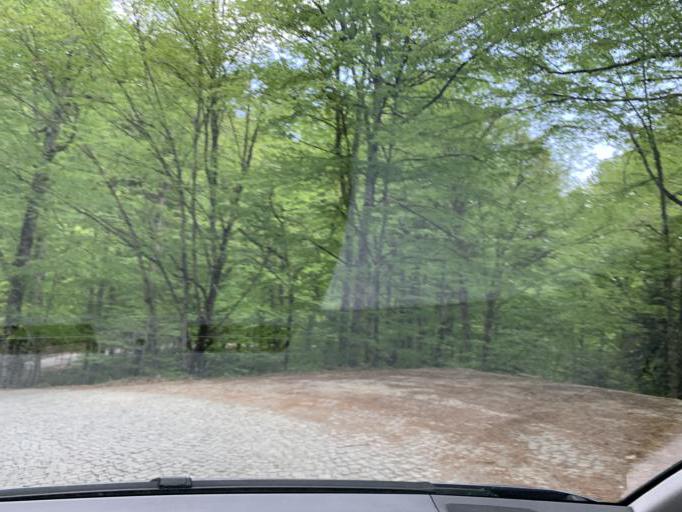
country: TR
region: Zonguldak
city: Egerci
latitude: 40.9362
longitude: 31.7412
